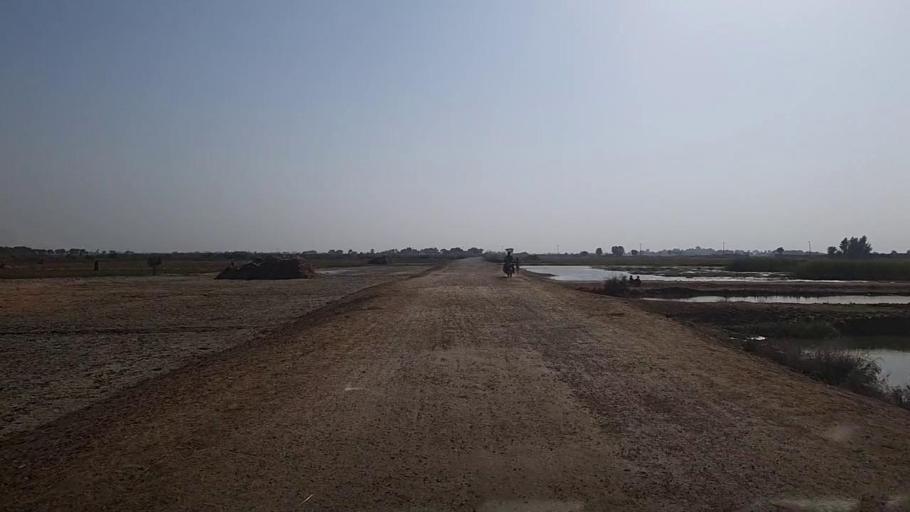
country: PK
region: Sindh
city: Kandhkot
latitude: 28.3874
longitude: 69.3380
